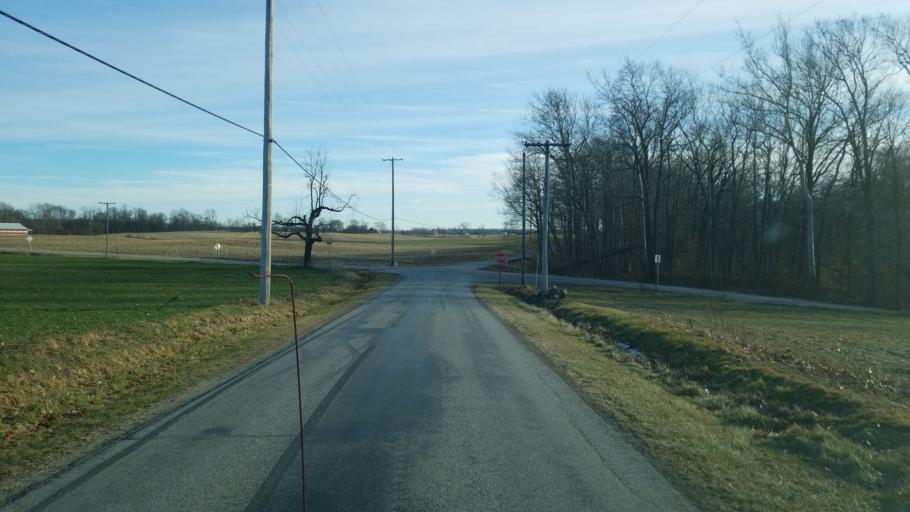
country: US
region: Ohio
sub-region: Huron County
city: Monroeville
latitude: 41.1761
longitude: -82.6967
